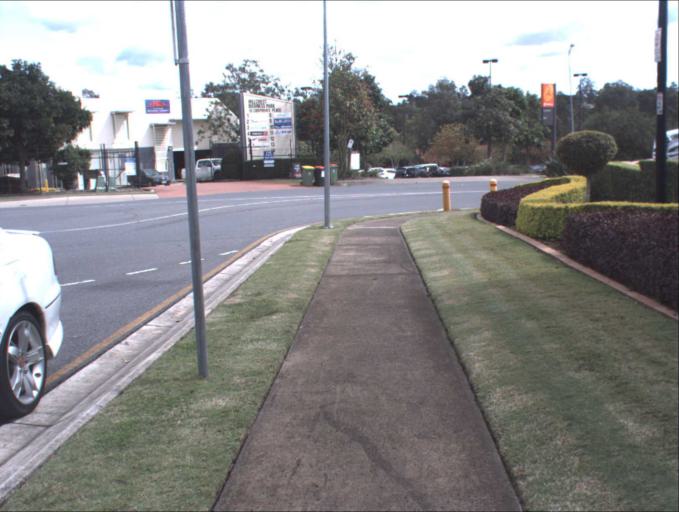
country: AU
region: Queensland
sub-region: Logan
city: Park Ridge South
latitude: -27.6695
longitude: 153.0308
